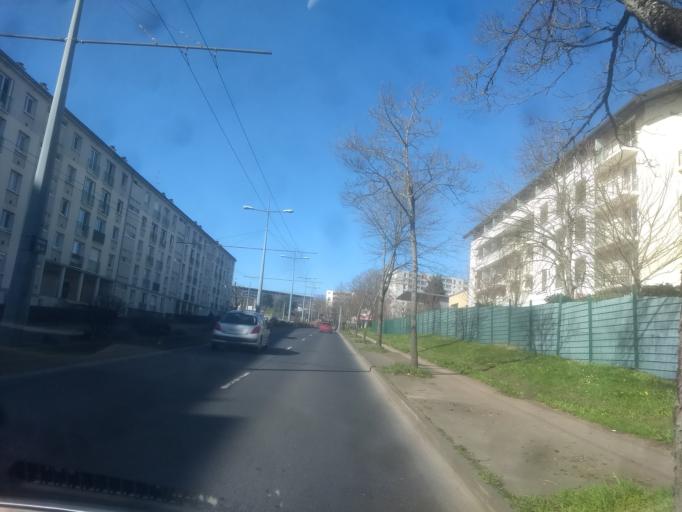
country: FR
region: Limousin
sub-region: Departement de la Haute-Vienne
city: Limoges
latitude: 45.8205
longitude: 1.2477
